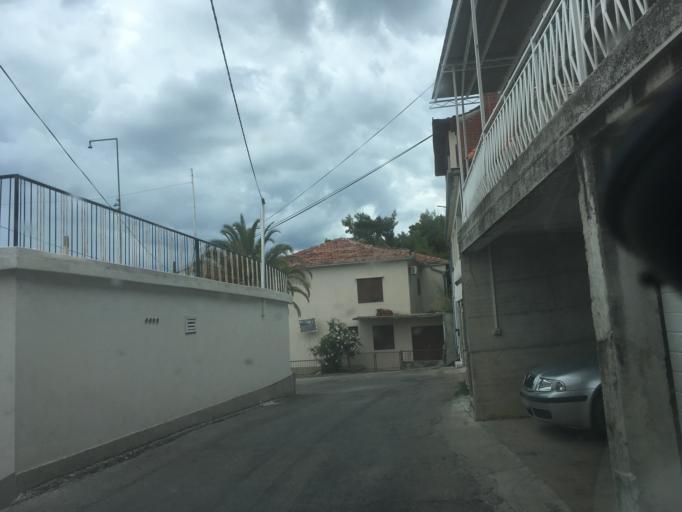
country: HR
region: Splitsko-Dalmatinska
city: Jesenice
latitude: 43.4520
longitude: 16.6268
